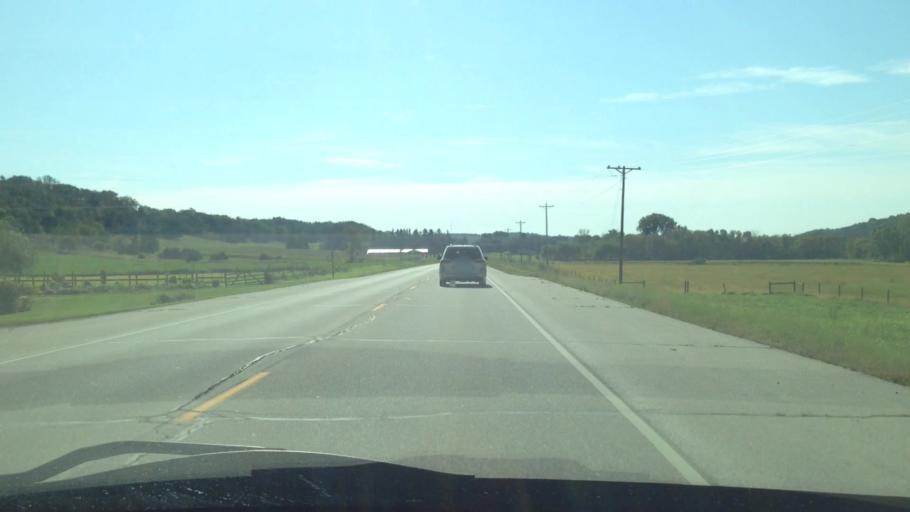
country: US
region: Minnesota
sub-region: Fillmore County
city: Chatfield
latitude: 43.8787
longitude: -92.2159
